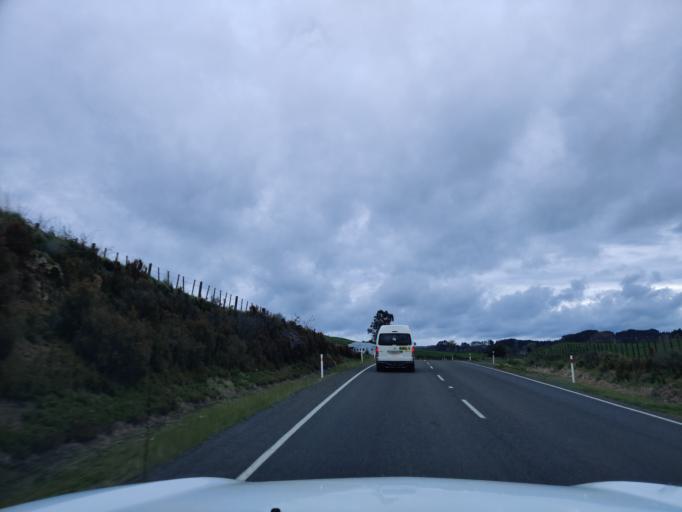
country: NZ
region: Waikato
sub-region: Otorohanga District
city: Otorohanga
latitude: -38.4553
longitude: 175.1660
